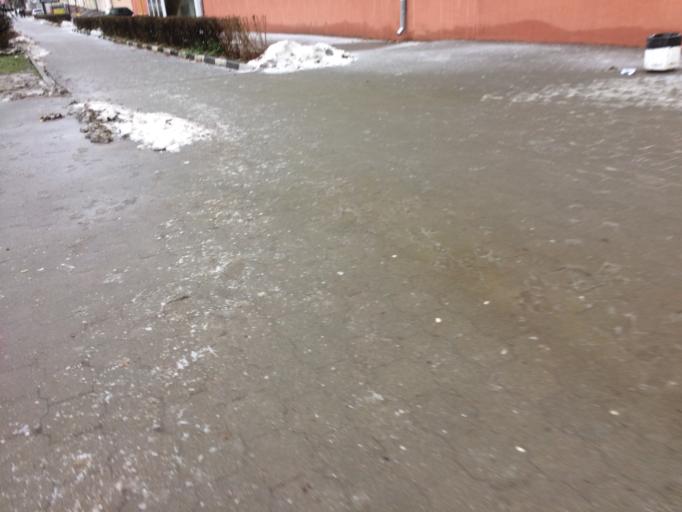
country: RU
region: Tula
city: Mendeleyevskiy
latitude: 54.1669
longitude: 37.5892
